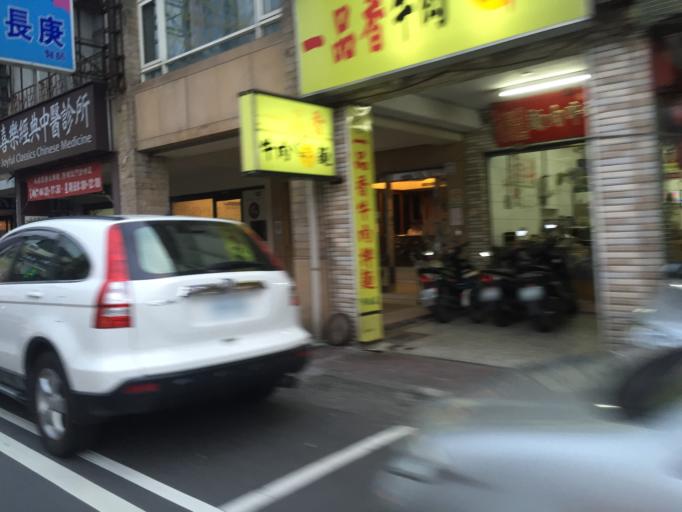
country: TW
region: Taiwan
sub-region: Yilan
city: Yilan
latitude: 24.7617
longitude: 121.7537
